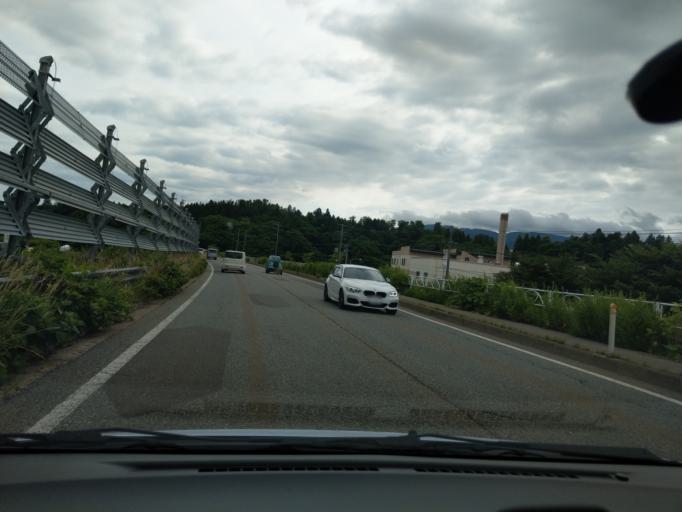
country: JP
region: Akita
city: Yokotemachi
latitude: 39.3321
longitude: 140.5586
